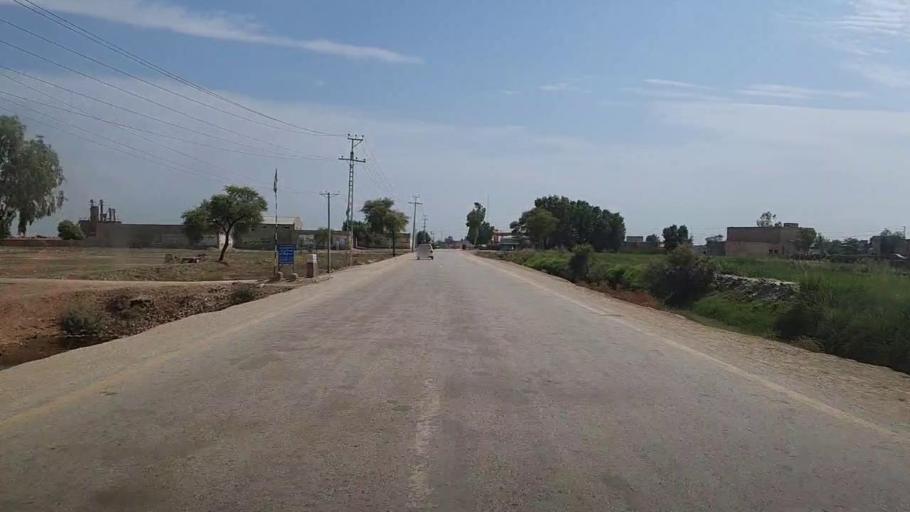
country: PK
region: Sindh
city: Thul
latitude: 28.2340
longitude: 68.7904
